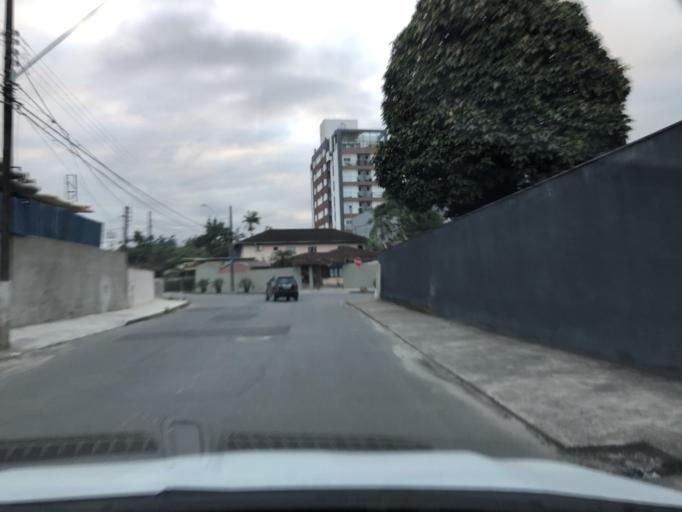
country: BR
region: Santa Catarina
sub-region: Joinville
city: Joinville
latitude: -26.2684
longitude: -48.8628
